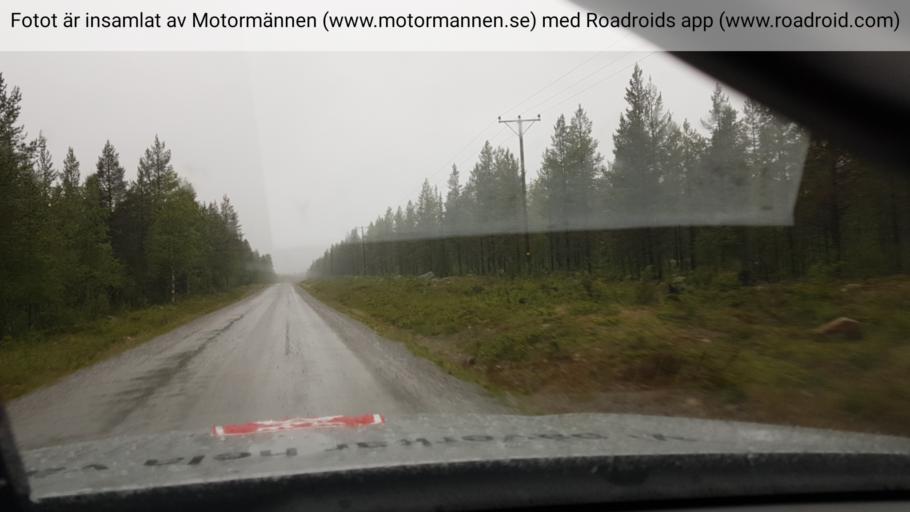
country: SE
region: Norrbotten
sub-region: Jokkmokks Kommun
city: Jokkmokk
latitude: 66.6123
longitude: 18.9587
